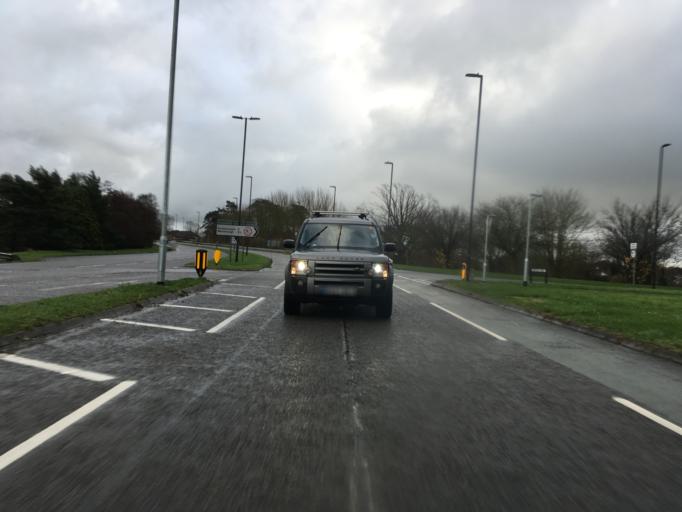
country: GB
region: England
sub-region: South Gloucestershire
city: Chipping Sodbury
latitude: 51.5353
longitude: -2.4021
